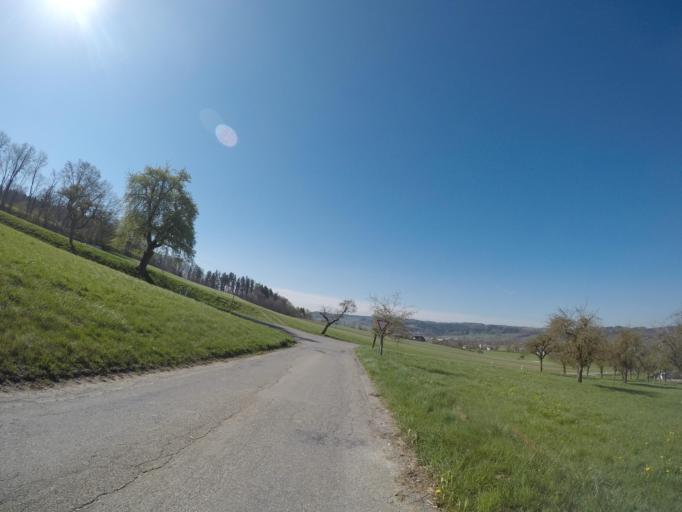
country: DE
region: Baden-Wuerttemberg
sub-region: Tuebingen Region
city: Wilhelmsdorf
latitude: 47.8694
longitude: 9.4459
